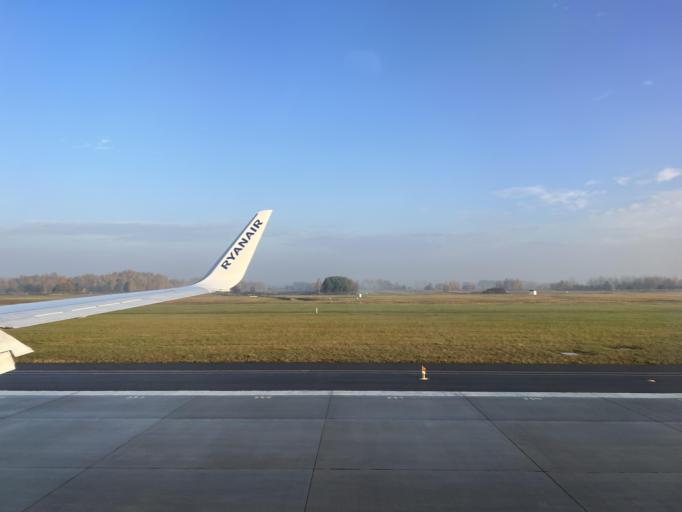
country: PL
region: Silesian Voivodeship
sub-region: Powiat tarnogorski
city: Ozarowice
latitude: 50.4761
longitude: 19.0772
